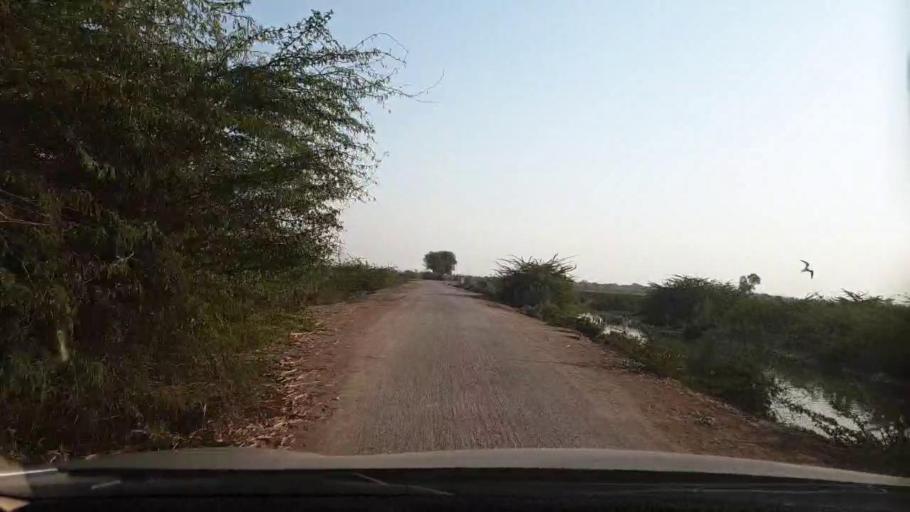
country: PK
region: Sindh
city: Berani
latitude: 25.6483
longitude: 68.8064
